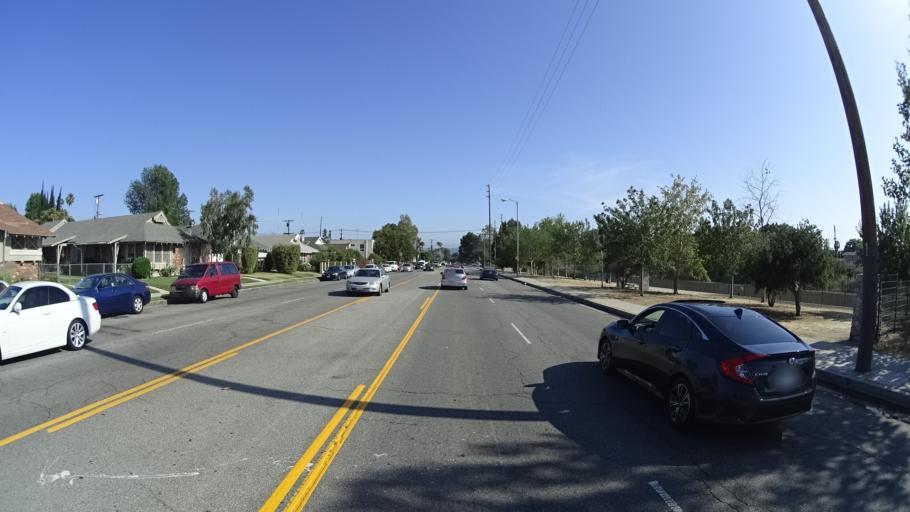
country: US
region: California
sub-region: Los Angeles County
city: Van Nuys
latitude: 34.1810
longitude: -118.4139
